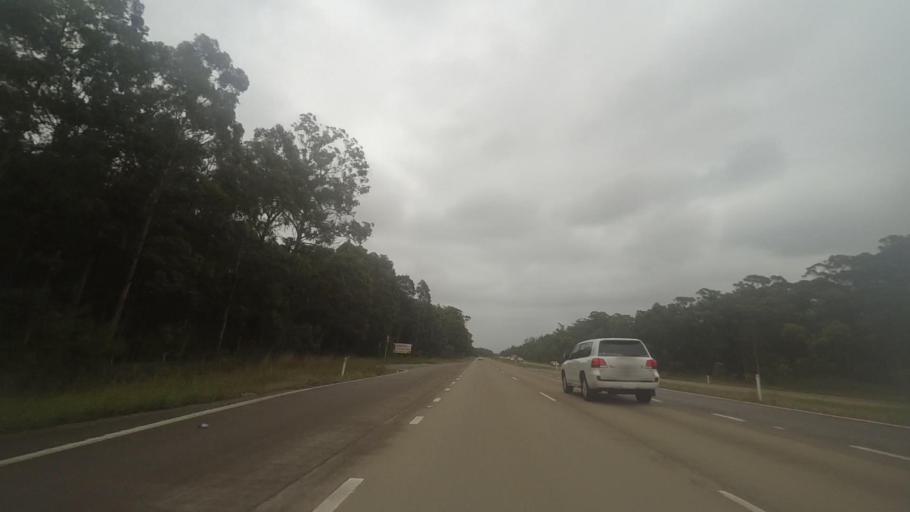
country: AU
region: New South Wales
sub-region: Port Stephens Shire
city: Medowie
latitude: -32.6510
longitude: 151.8981
